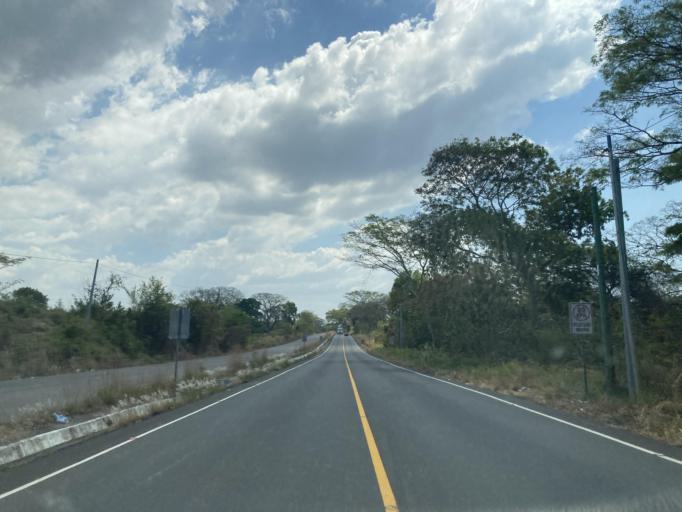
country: GT
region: Santa Rosa
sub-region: Municipio de Taxisco
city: Taxisco
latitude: 14.0966
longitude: -90.5301
